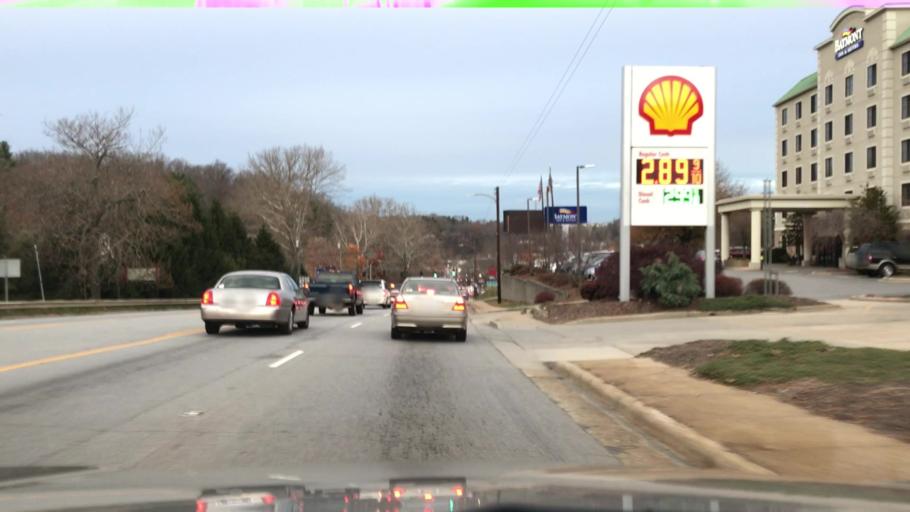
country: US
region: North Carolina
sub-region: Buncombe County
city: Biltmore Forest
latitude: 35.5618
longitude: -82.5409
